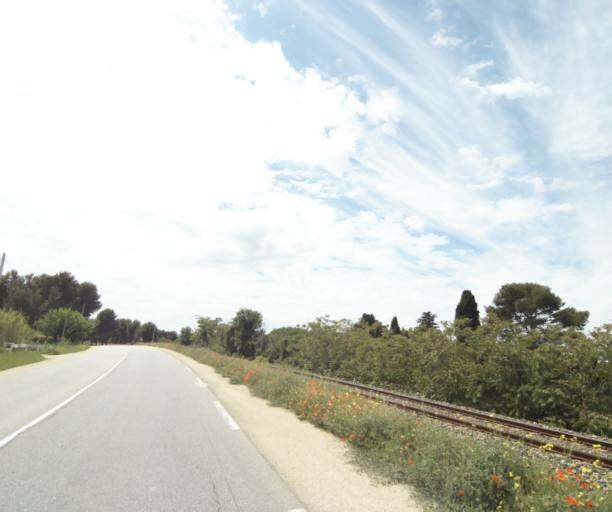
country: FR
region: Provence-Alpes-Cote d'Azur
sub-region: Departement des Bouches-du-Rhone
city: Rognac
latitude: 43.4999
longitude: 5.2328
